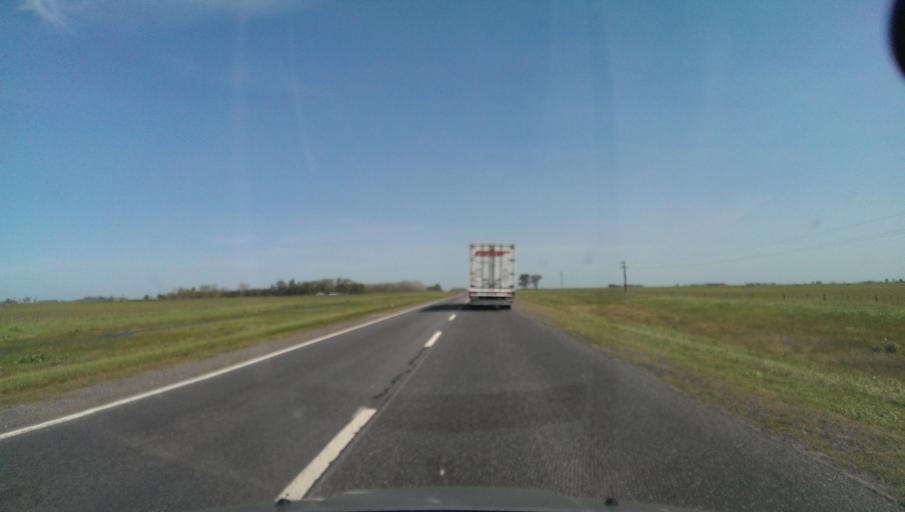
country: AR
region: Buenos Aires
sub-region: Partido de Azul
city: Azul
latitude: -36.5613
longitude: -59.6381
